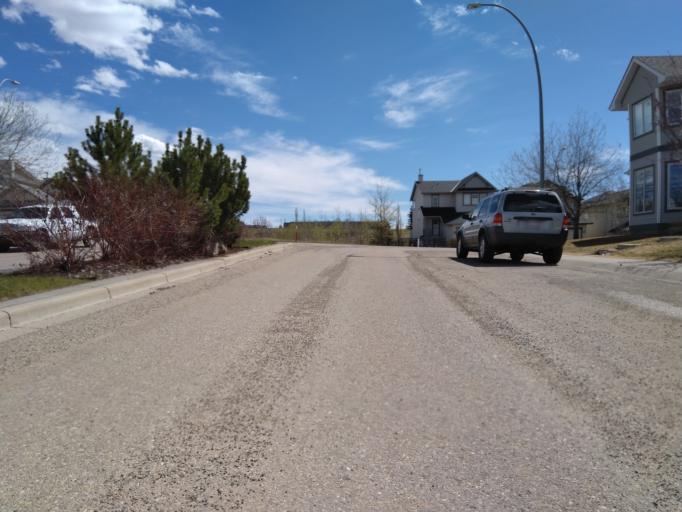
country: CA
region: Alberta
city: Calgary
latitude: 51.1319
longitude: -114.2424
